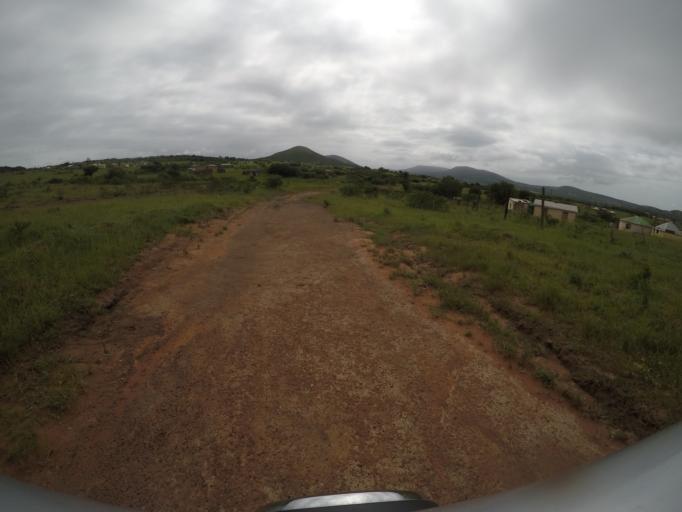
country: ZA
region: KwaZulu-Natal
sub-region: uThungulu District Municipality
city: Empangeni
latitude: -28.6128
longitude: 31.8411
